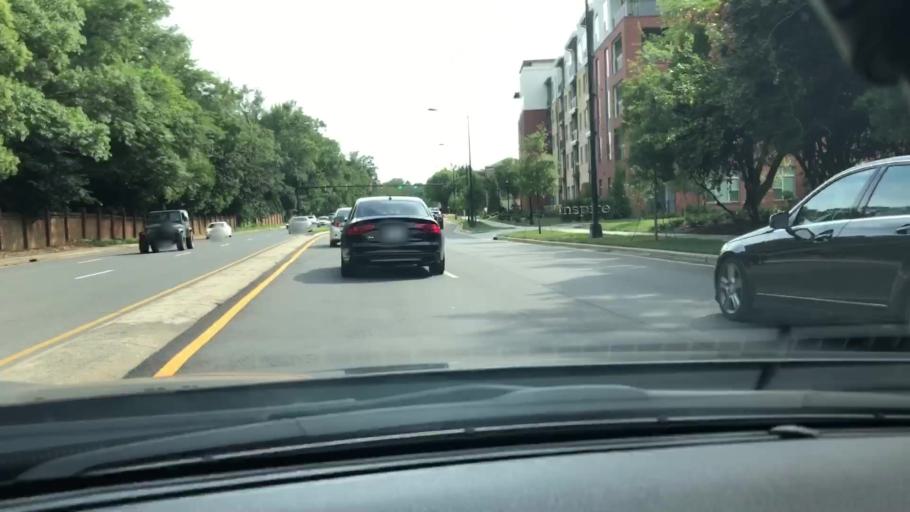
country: US
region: North Carolina
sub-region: Mecklenburg County
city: Charlotte
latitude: 35.1580
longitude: -80.8219
